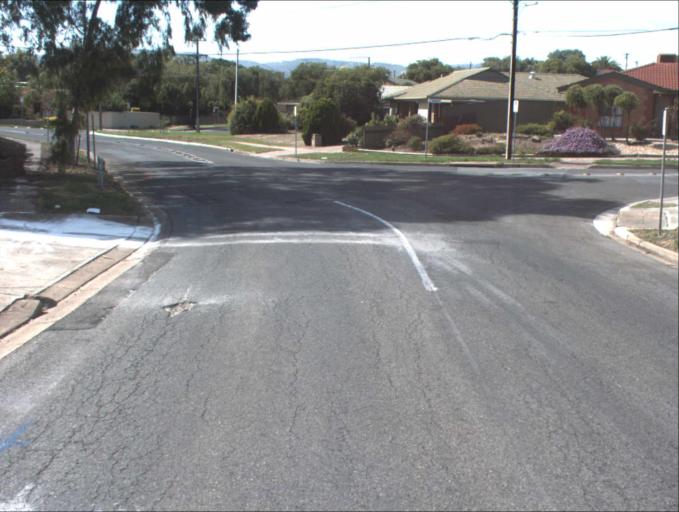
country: AU
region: South Australia
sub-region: Port Adelaide Enfield
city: Gilles Plains
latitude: -34.8642
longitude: 138.6528
